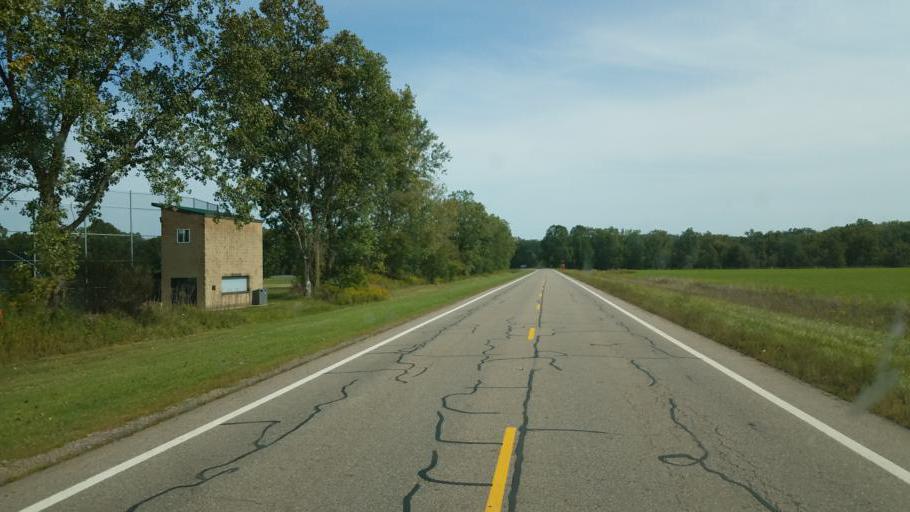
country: US
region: Ohio
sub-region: Knox County
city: Gambier
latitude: 40.3652
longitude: -82.3920
